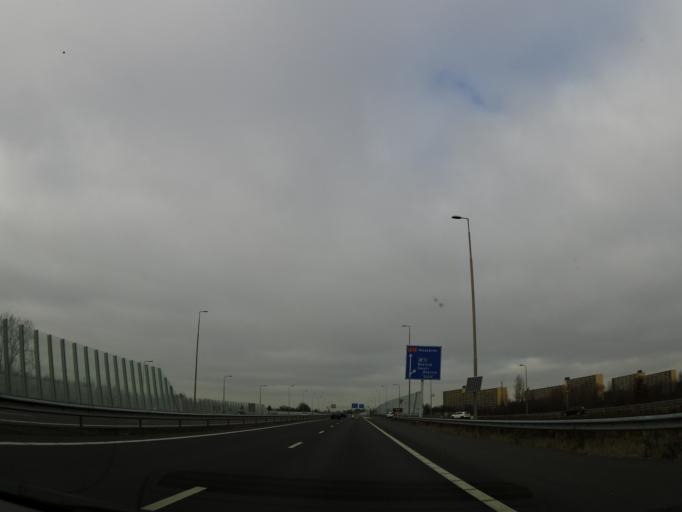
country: NL
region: Limburg
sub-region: Gemeente Venlo
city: Tegelen
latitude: 51.3542
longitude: 6.1491
